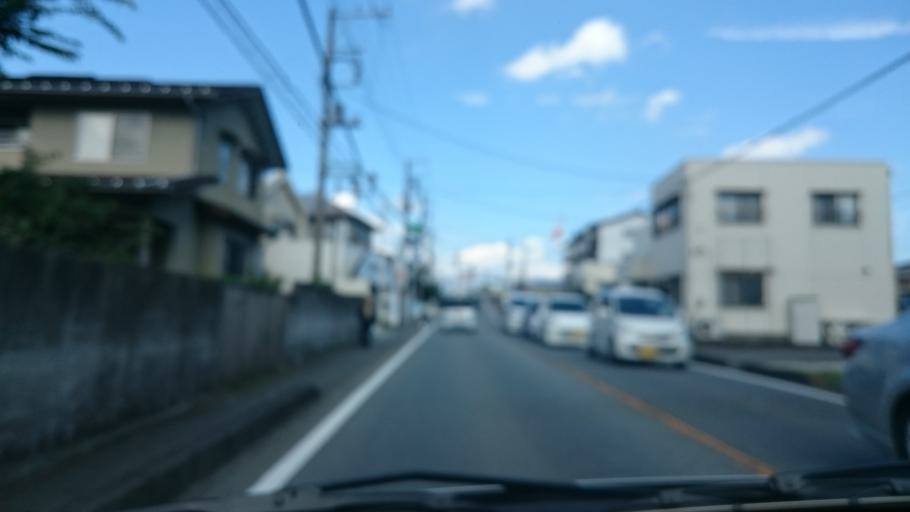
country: JP
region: Shizuoka
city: Gotemba
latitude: 35.2557
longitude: 138.9218
